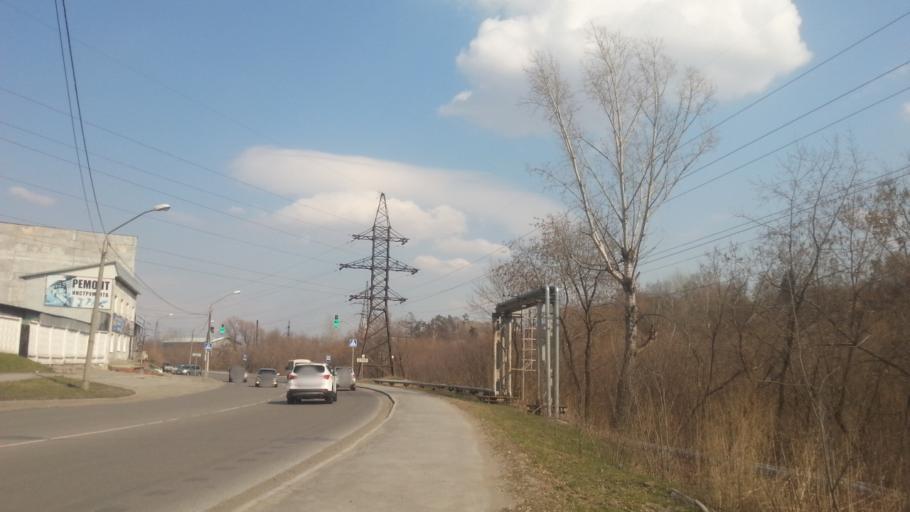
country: RU
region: Altai Krai
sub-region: Gorod Barnaulskiy
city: Barnaul
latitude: 53.3168
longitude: 83.7574
